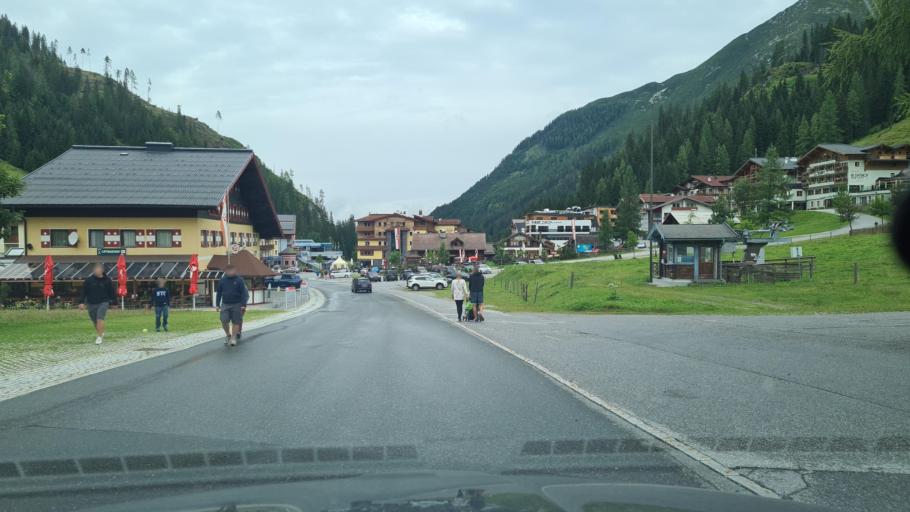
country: AT
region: Salzburg
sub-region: Politischer Bezirk Sankt Johann im Pongau
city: Untertauern
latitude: 47.2915
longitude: 13.4570
